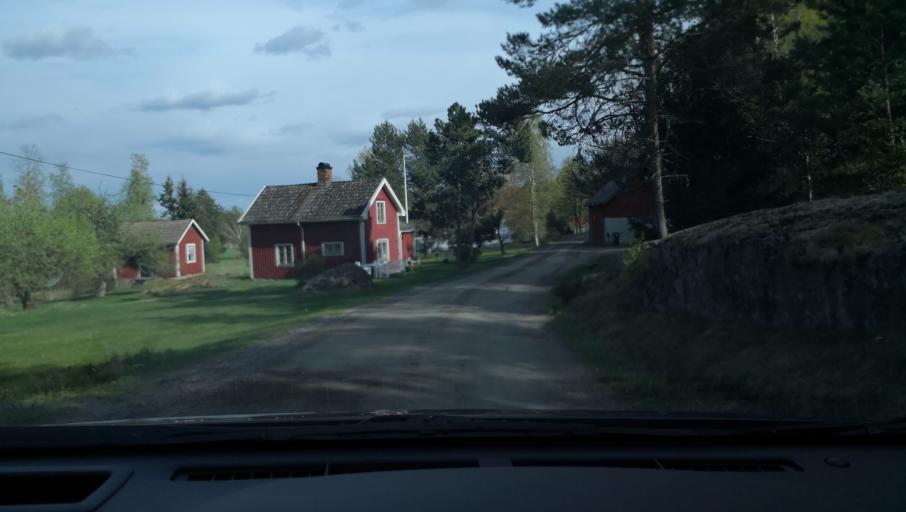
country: SE
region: OErebro
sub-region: Askersunds Kommun
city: Asbro
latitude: 59.0298
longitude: 15.0516
